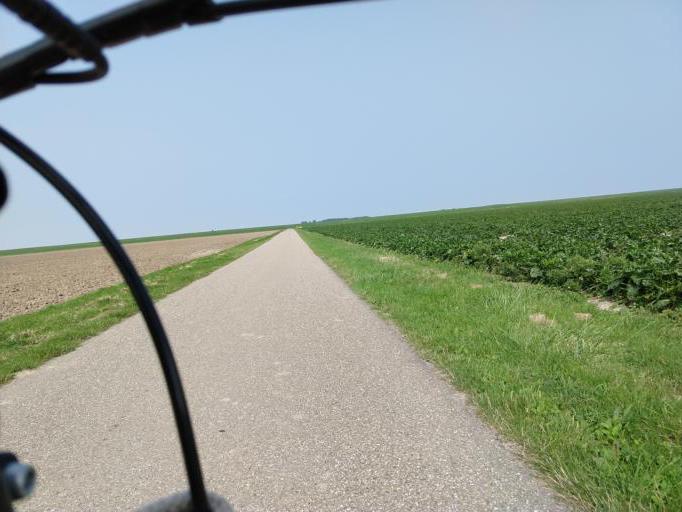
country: NL
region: Zeeland
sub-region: Gemeente Goes
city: Goes
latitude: 51.5362
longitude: 3.8756
